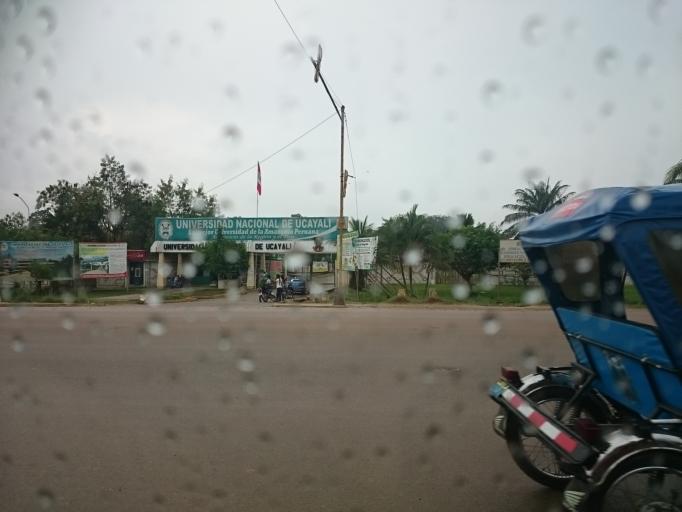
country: PE
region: Ucayali
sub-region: Provincia de Coronel Portillo
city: Pucallpa
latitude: -8.3916
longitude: -74.5786
